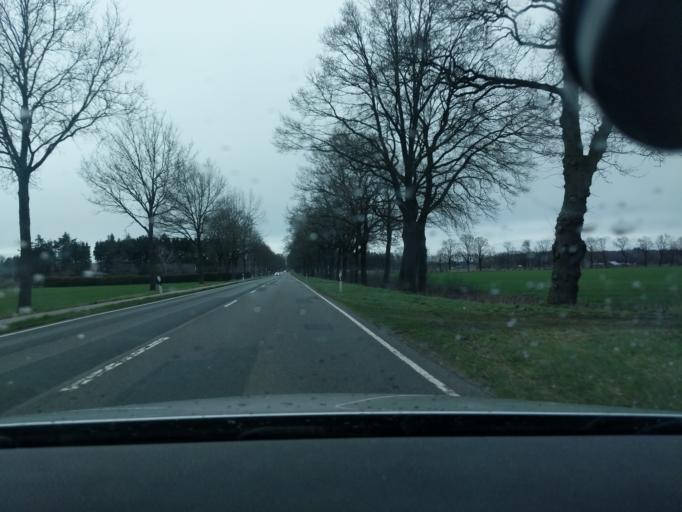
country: DE
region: Lower Saxony
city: Bremervorde
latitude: 53.5070
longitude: 9.1942
